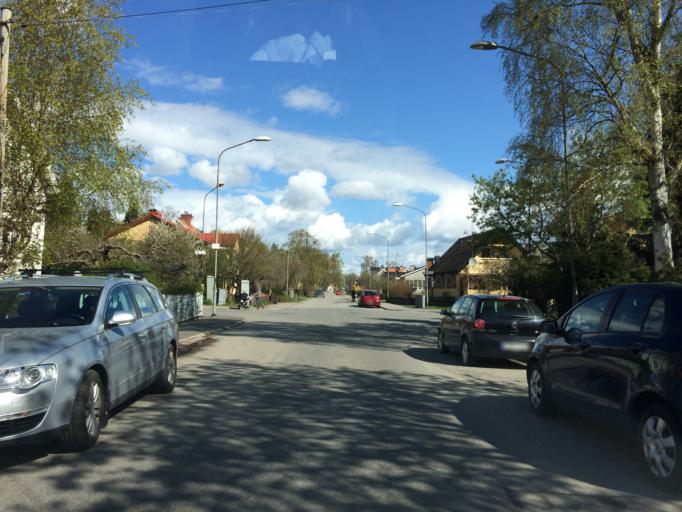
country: SE
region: Stockholm
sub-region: Huddinge Kommun
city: Segeltorp
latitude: 59.2960
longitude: 17.9479
